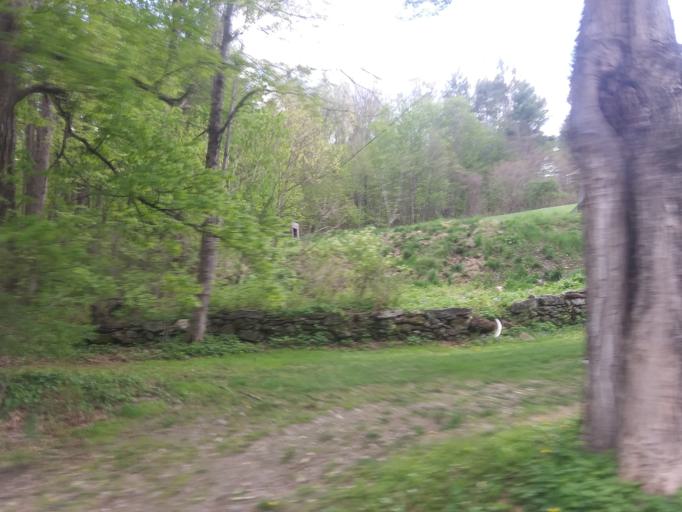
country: US
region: Massachusetts
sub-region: Franklin County
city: Buckland
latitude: 42.5655
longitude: -72.8054
